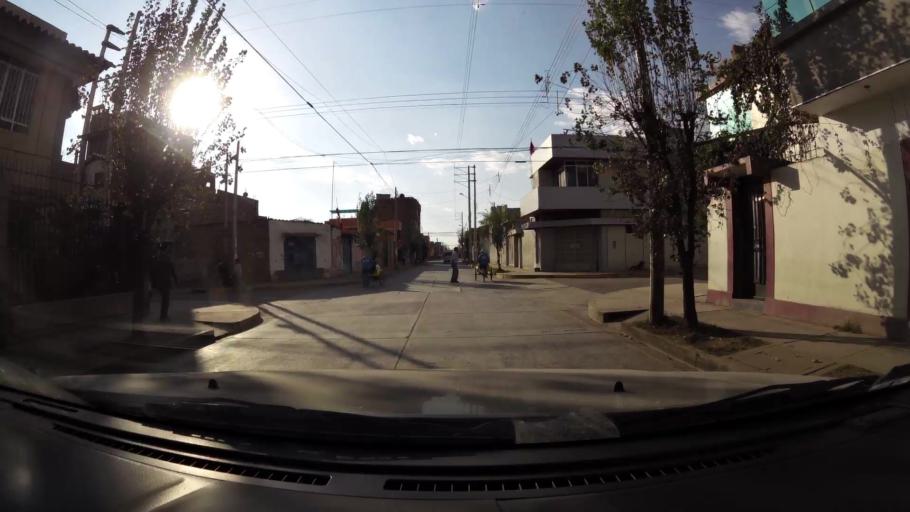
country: PE
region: Junin
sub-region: Provincia de Huancayo
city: El Tambo
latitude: -12.0519
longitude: -75.2186
